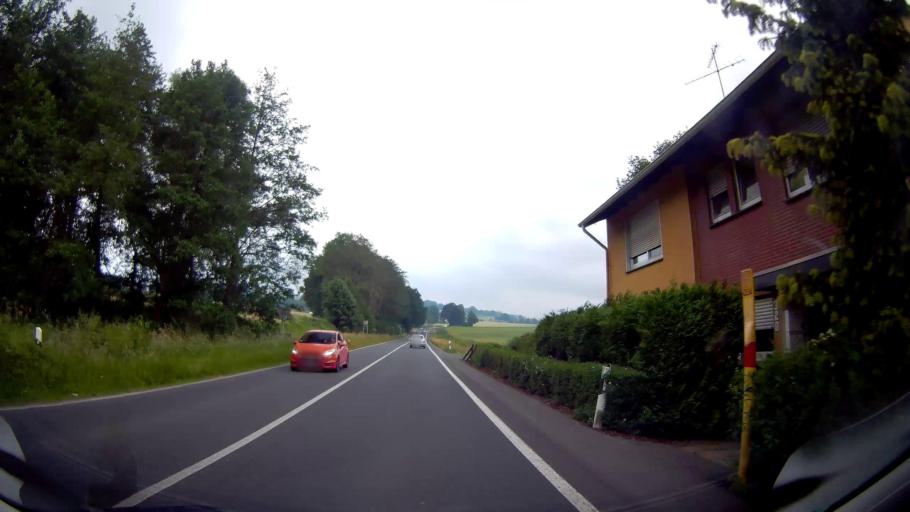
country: DE
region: North Rhine-Westphalia
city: Loehne
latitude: 52.1595
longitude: 8.7336
